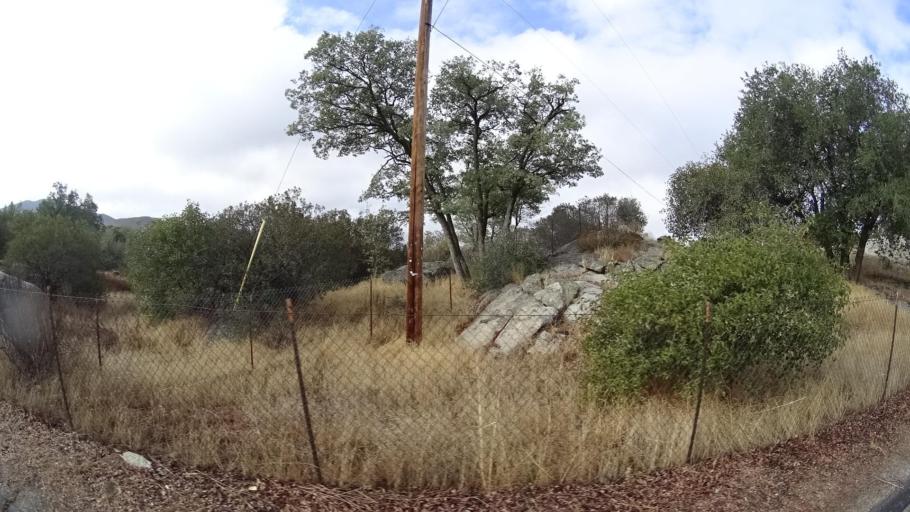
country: MX
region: Baja California
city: Tecate
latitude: 32.6382
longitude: -116.6364
